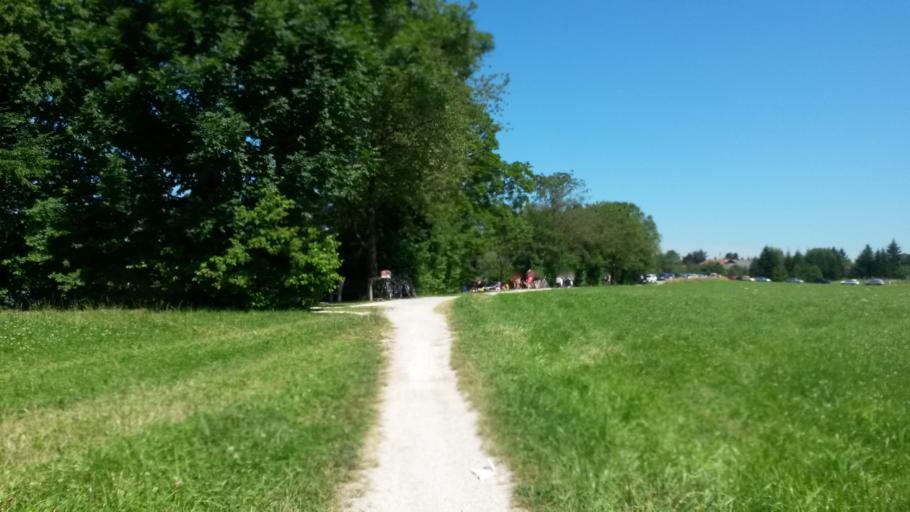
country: DE
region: Bavaria
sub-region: Upper Bavaria
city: Grassau
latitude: 47.7734
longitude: 12.4620
